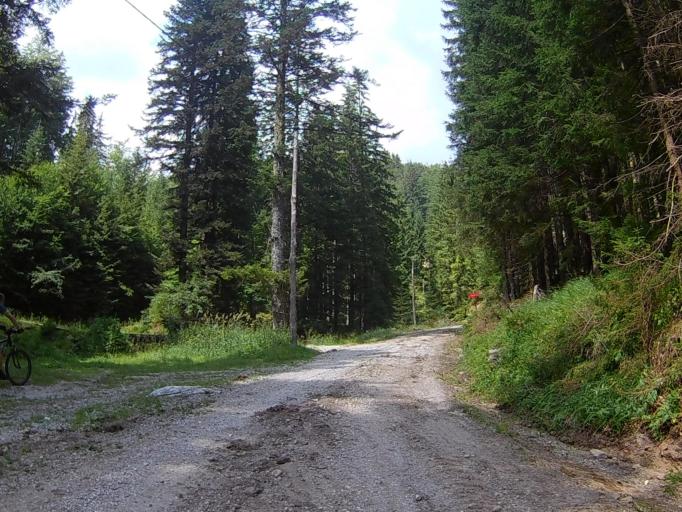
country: SI
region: Lovrenc na Pohorju
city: Lovrenc na Pohorju
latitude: 46.4807
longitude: 15.4332
